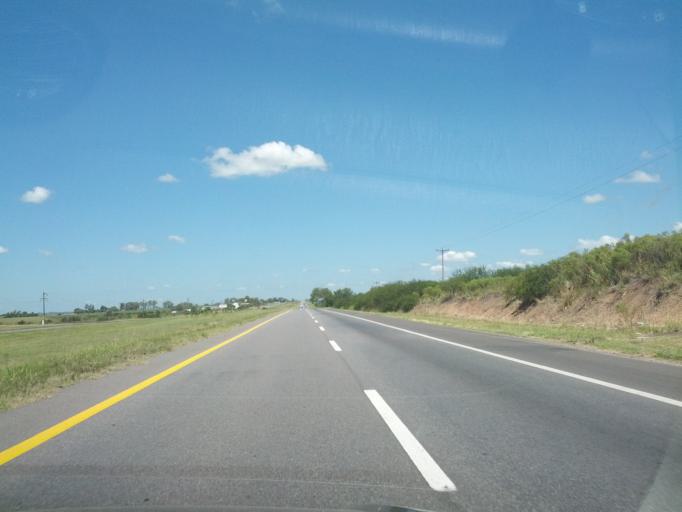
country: AR
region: Entre Rios
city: Gualeguaychu
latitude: -33.0914
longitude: -58.6404
